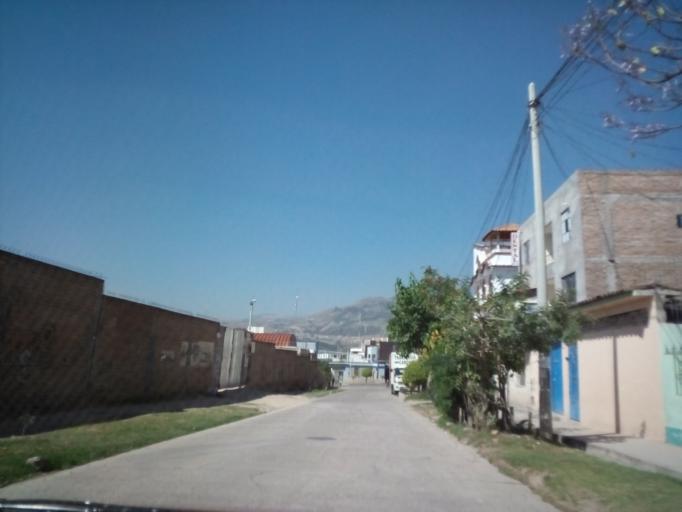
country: PE
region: Ayacucho
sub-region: Provincia de Huamanga
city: Ayacucho
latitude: -13.1492
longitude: -74.2248
